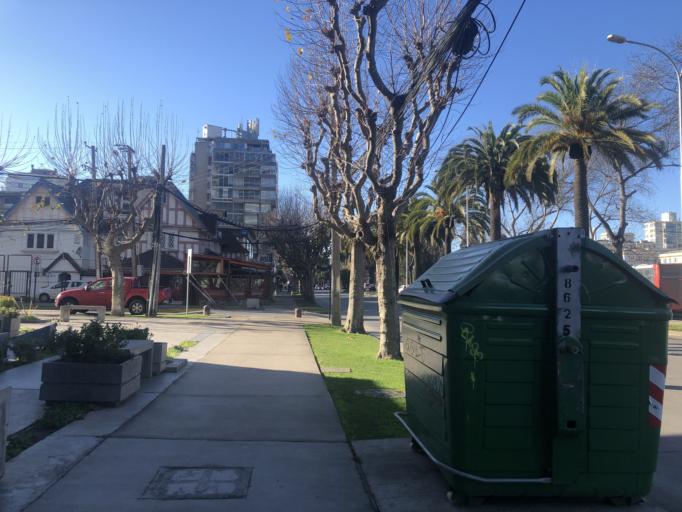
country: CL
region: Valparaiso
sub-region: Provincia de Valparaiso
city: Vina del Mar
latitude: -33.0222
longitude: -71.5531
